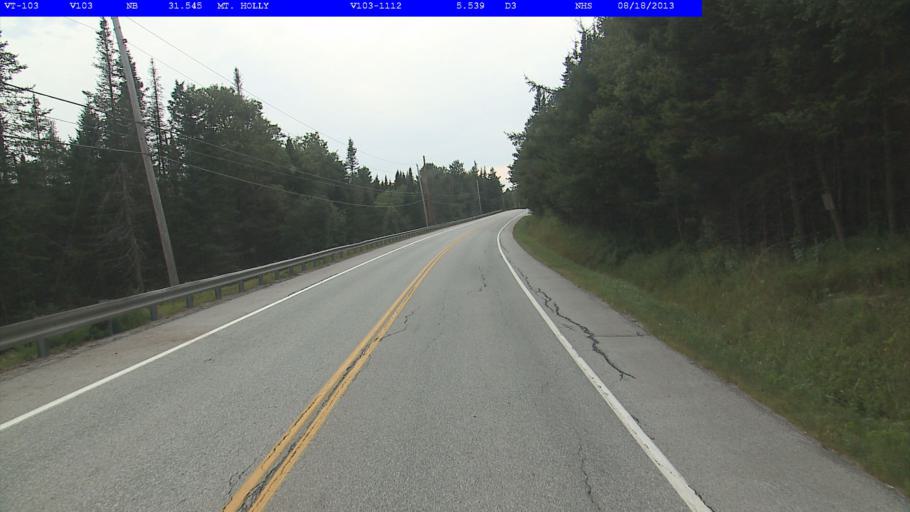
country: US
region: Vermont
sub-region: Rutland County
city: Rutland
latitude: 43.4475
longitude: -72.8312
